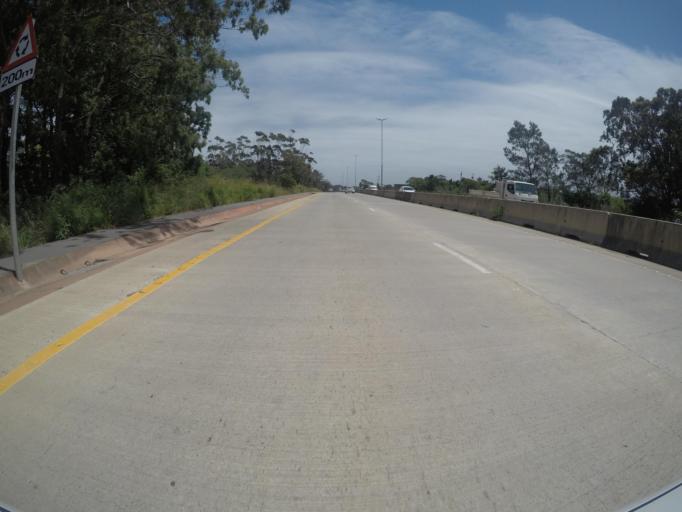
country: ZA
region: Eastern Cape
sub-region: Buffalo City Metropolitan Municipality
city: East London
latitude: -32.9417
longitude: 27.9627
